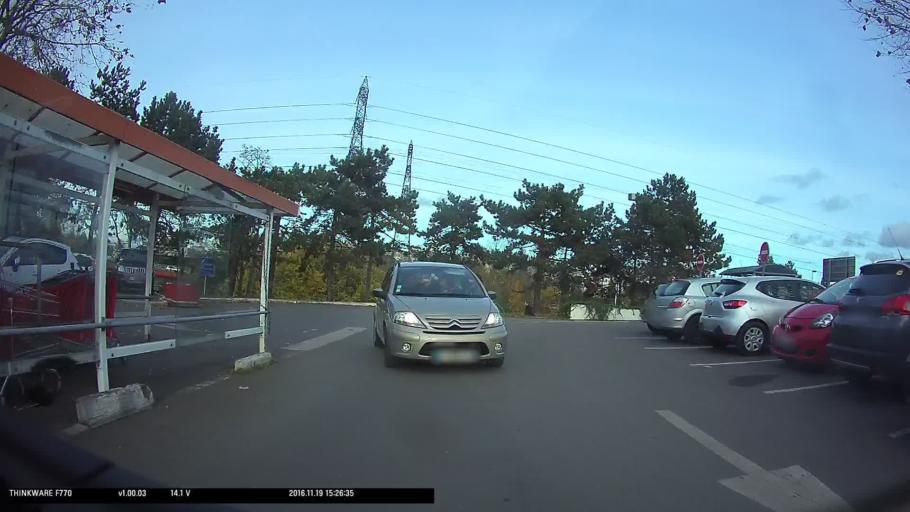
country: FR
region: Ile-de-France
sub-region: Departement du Val-d'Oise
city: Cergy-Pontoise
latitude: 49.0398
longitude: 2.0802
